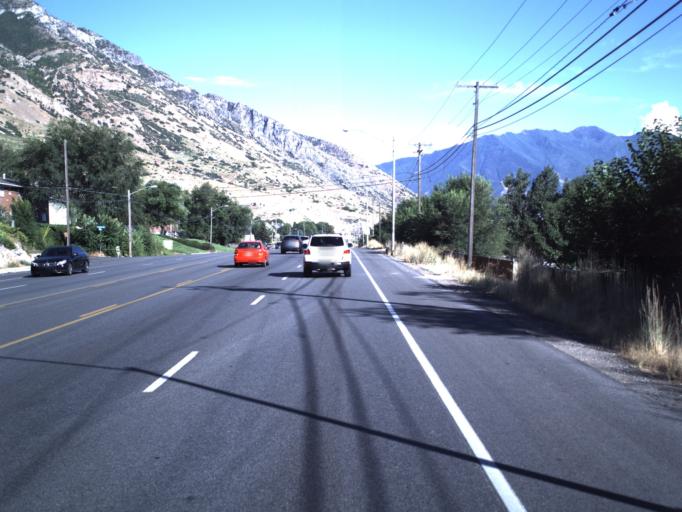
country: US
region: Utah
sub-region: Utah County
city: Provo
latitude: 40.2055
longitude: -111.6272
